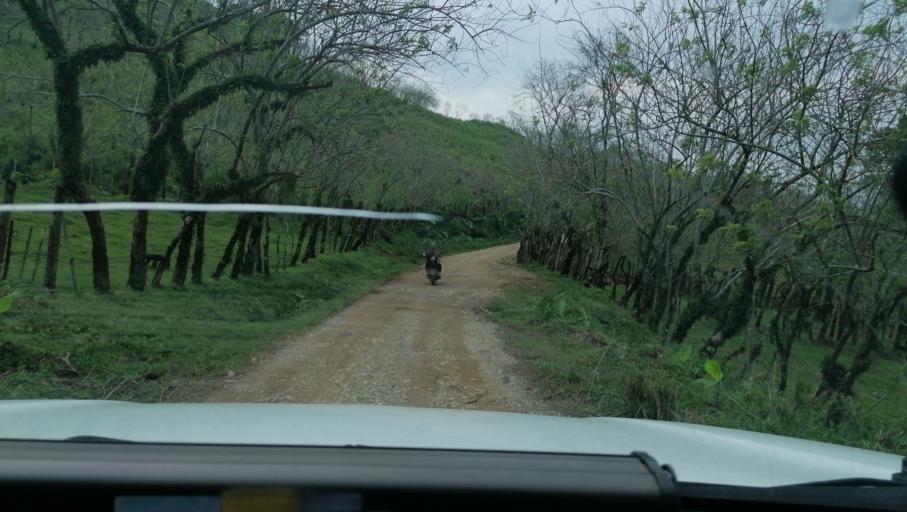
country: MX
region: Chiapas
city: Ixtacomitan
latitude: 17.3371
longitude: -93.1130
